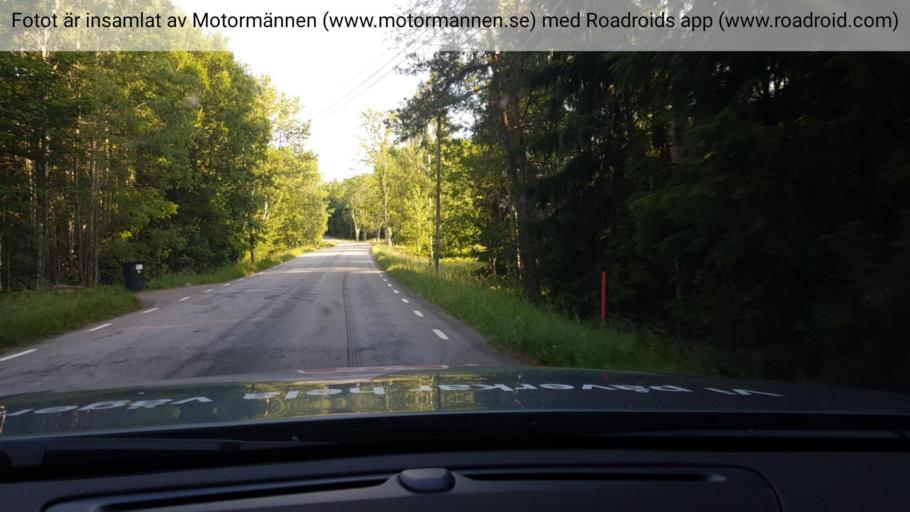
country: SE
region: Uppsala
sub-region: Osthammars Kommun
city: Gimo
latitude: 59.9796
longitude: 18.0616
